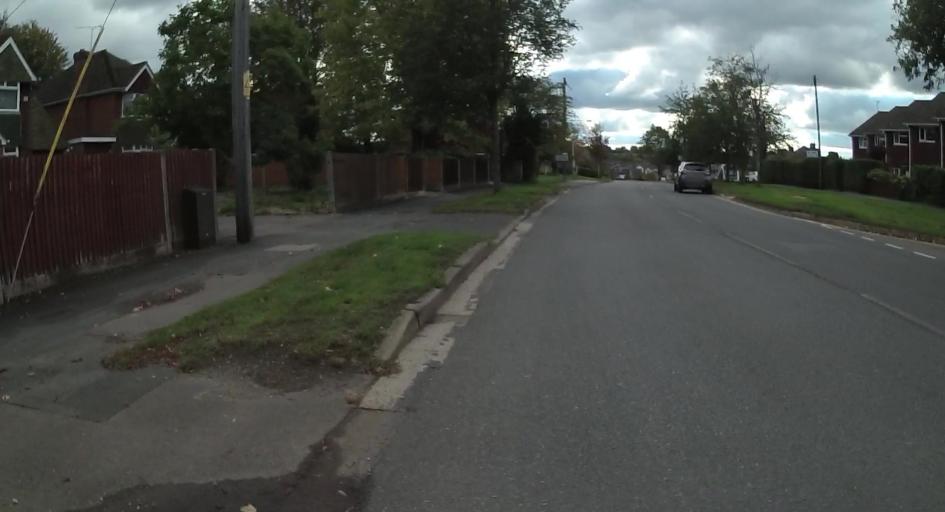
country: GB
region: England
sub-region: Surrey
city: Seale
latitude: 51.2389
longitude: -0.7299
